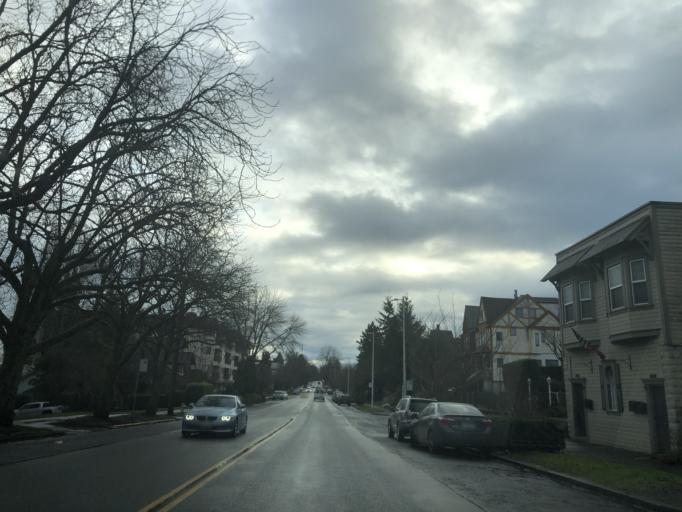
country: US
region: Washington
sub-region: Pierce County
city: Tacoma
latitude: 47.2662
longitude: -122.4636
